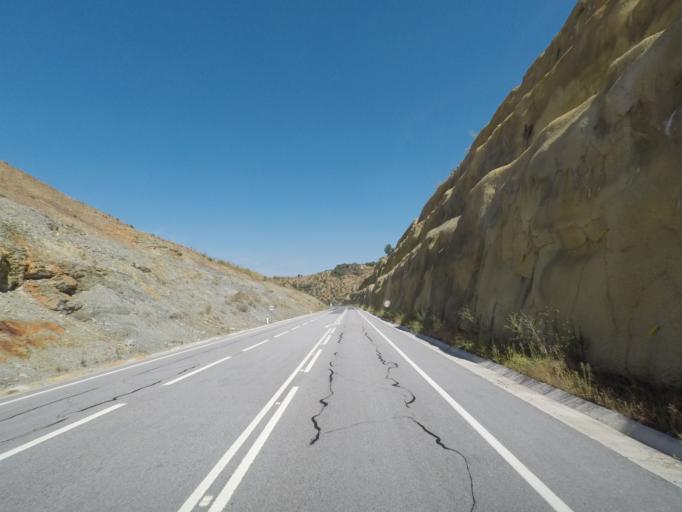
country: PT
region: Braganca
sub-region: Alfandega da Fe
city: Alfandega da Fe
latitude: 41.2916
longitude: -6.8958
